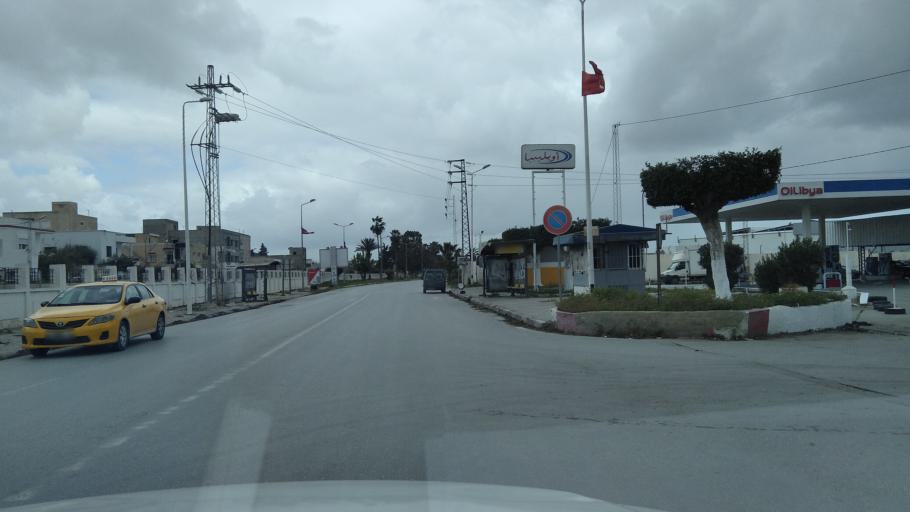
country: TN
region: Bin 'Arus
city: Ben Arous
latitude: 36.7570
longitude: 10.2192
